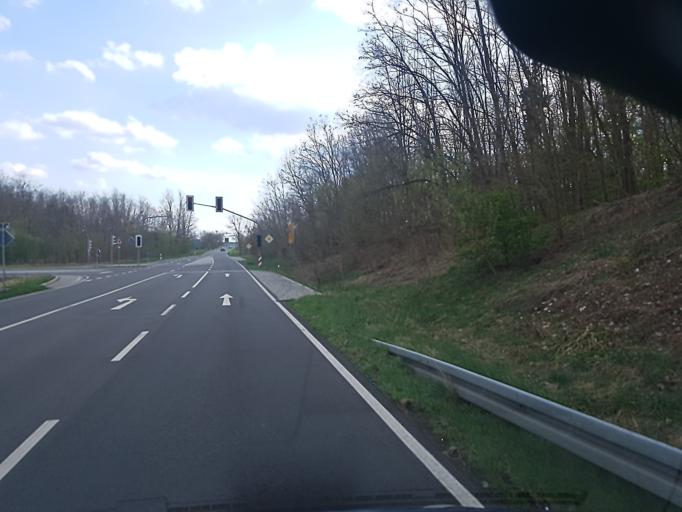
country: DE
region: Saxony-Anhalt
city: Grafenhainichen
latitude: 51.7252
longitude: 12.4287
